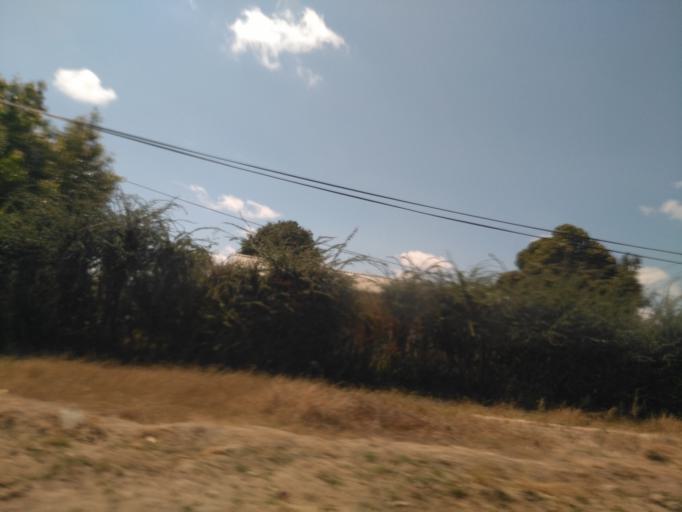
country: TZ
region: Dodoma
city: Dodoma
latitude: -6.1674
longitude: 35.7635
